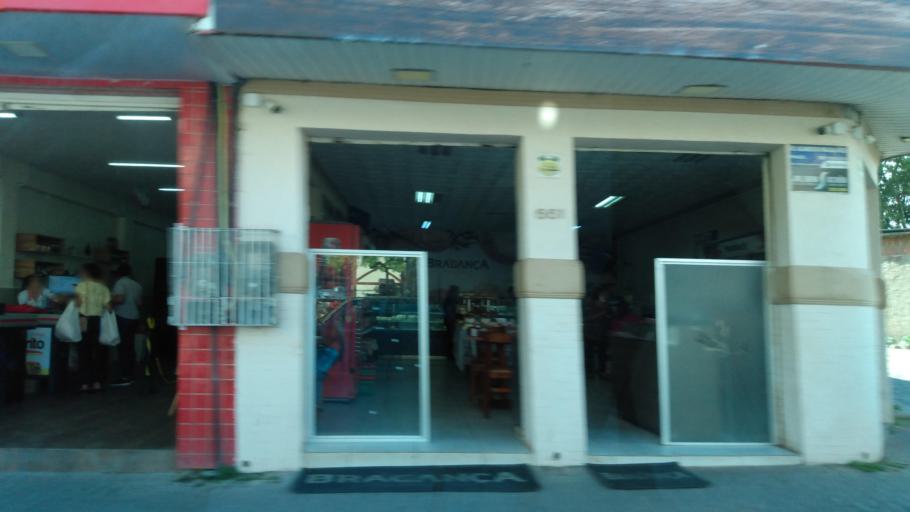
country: ET
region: Oromiya
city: Gore
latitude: 8.1981
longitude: 35.5612
